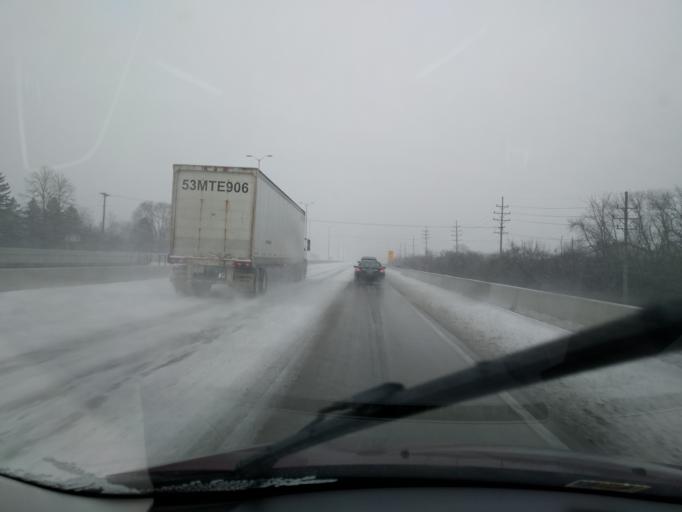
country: US
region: Wisconsin
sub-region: Waukesha County
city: Butler
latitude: 43.1341
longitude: -88.0308
